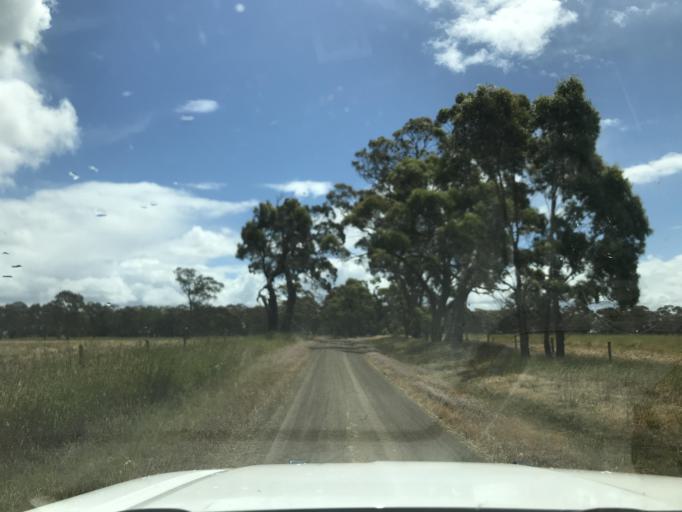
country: AU
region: South Australia
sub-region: Wattle Range
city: Penola
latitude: -37.1253
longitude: 141.2994
